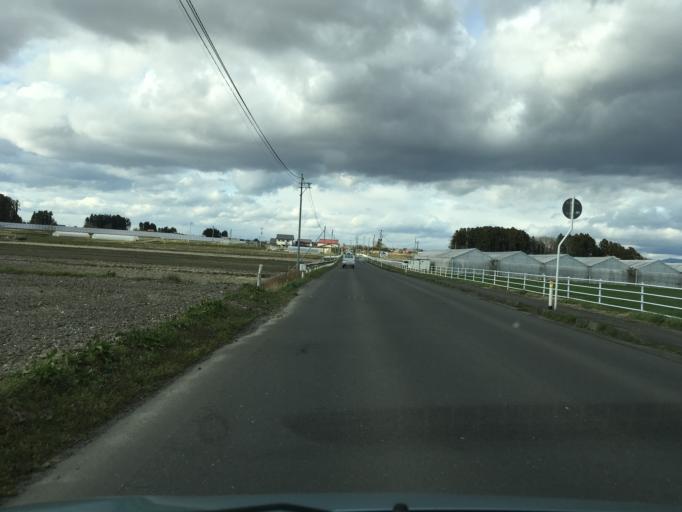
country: JP
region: Miyagi
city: Wakuya
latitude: 38.6536
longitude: 141.1918
